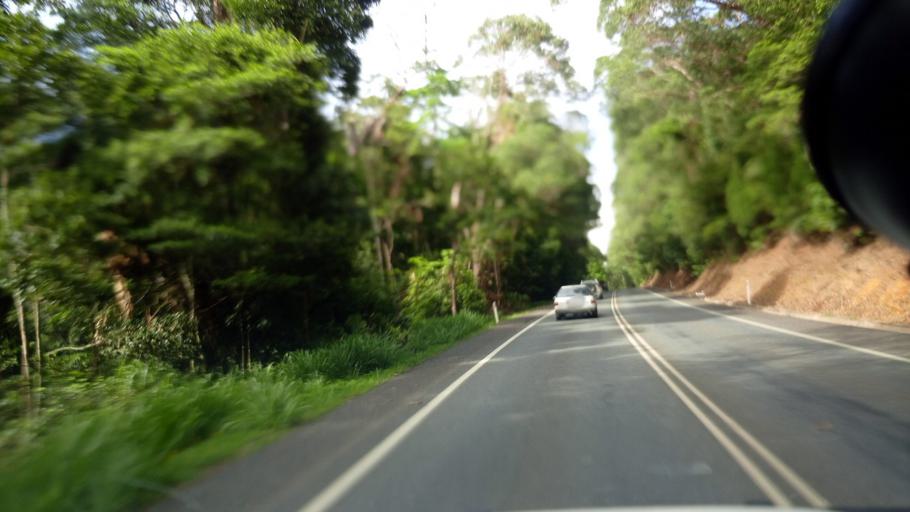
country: AU
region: Queensland
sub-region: Tablelands
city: Kuranda
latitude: -16.8197
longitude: 145.6308
